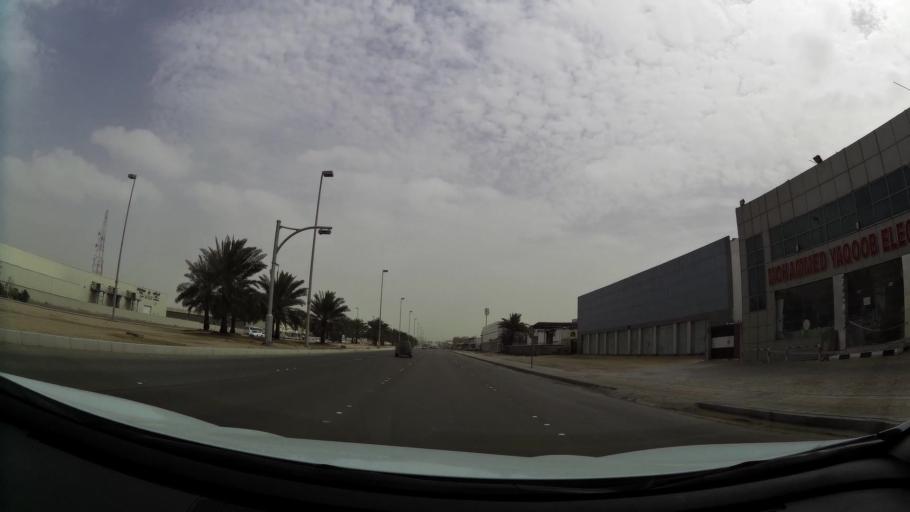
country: AE
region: Abu Dhabi
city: Abu Dhabi
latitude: 24.3724
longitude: 54.4935
